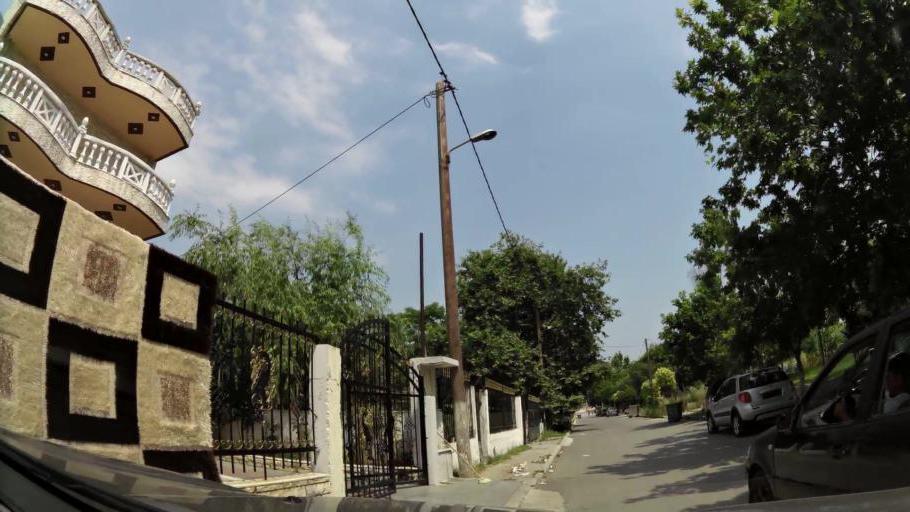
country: GR
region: Central Macedonia
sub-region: Nomos Thessalonikis
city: Menemeni
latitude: 40.6563
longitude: 22.8971
